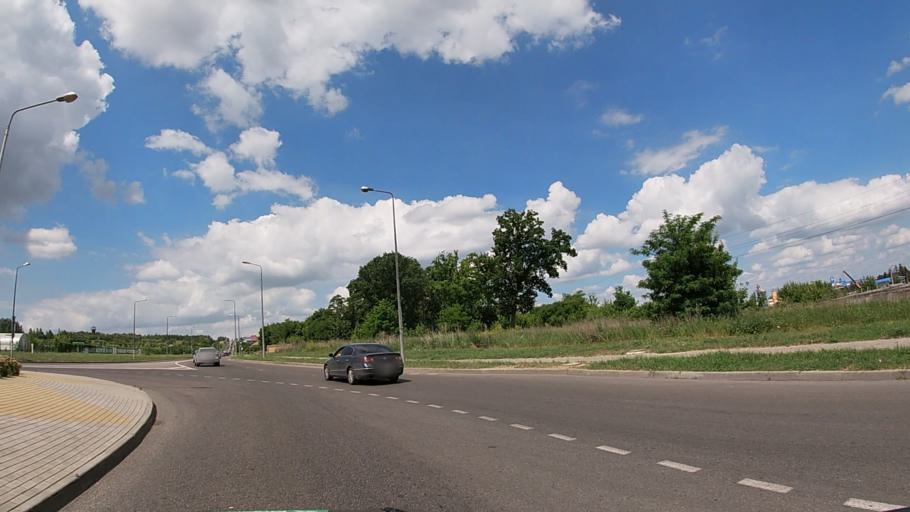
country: RU
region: Belgorod
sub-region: Belgorodskiy Rayon
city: Belgorod
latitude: 50.5952
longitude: 36.5520
